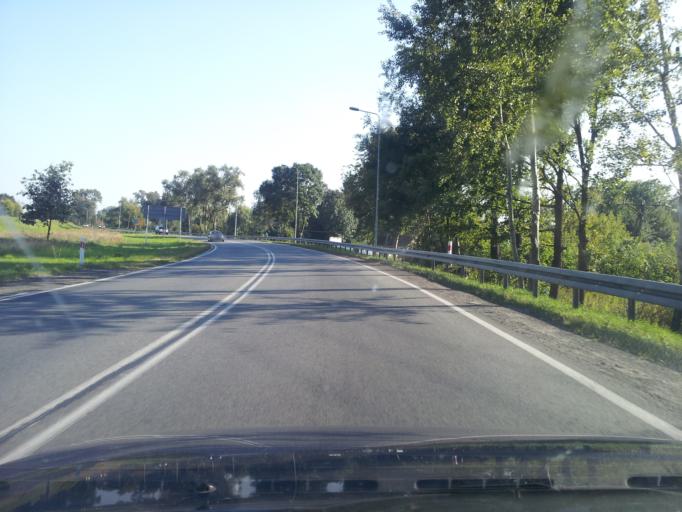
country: PL
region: Masovian Voivodeship
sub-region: Powiat nowodworski
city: Nowy Dwor Mazowiecki
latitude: 52.4197
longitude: 20.6867
